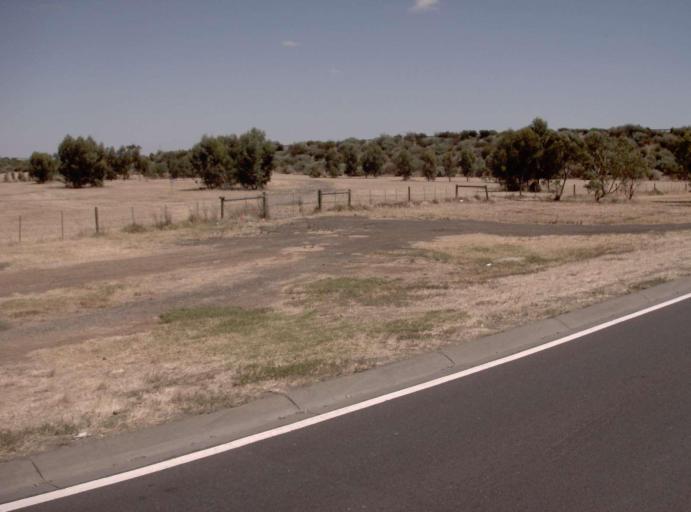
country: AU
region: Victoria
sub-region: Brimbank
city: Derrimut
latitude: -37.7988
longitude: 144.7889
